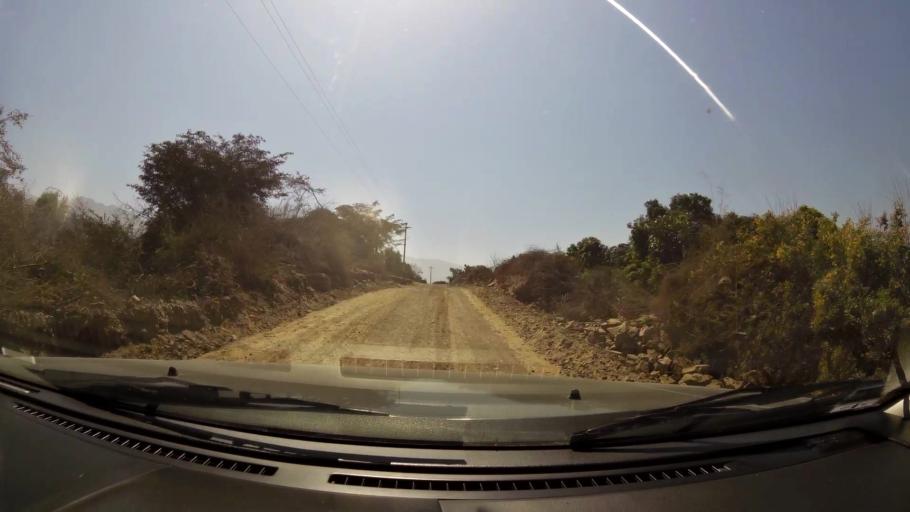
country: PE
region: Ica
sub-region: Provincia de Ica
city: Guadalupe
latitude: -13.8830
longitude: -75.6497
